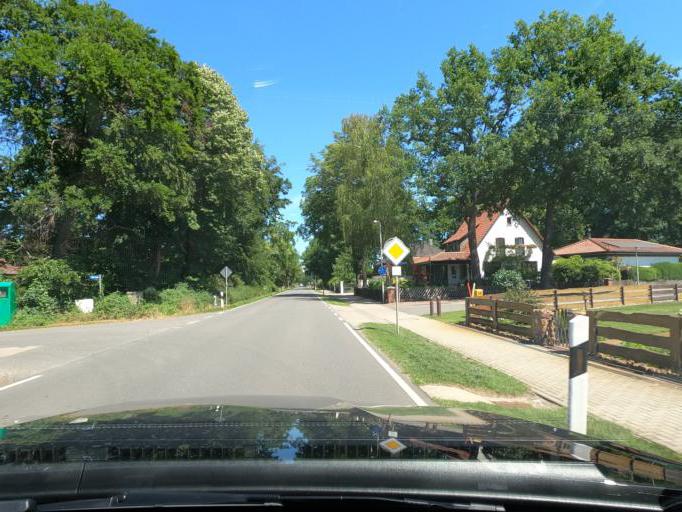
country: DE
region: Lower Saxony
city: Haenigsen
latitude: 52.4918
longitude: 10.1140
